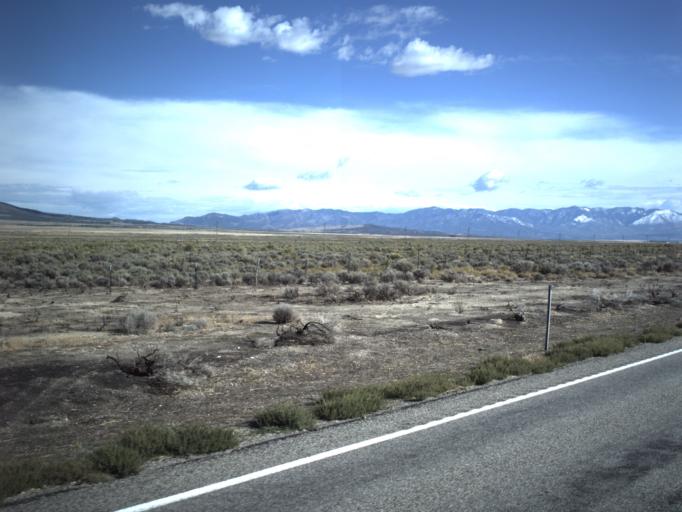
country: US
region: Utah
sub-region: Millard County
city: Delta
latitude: 39.2679
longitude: -112.4525
